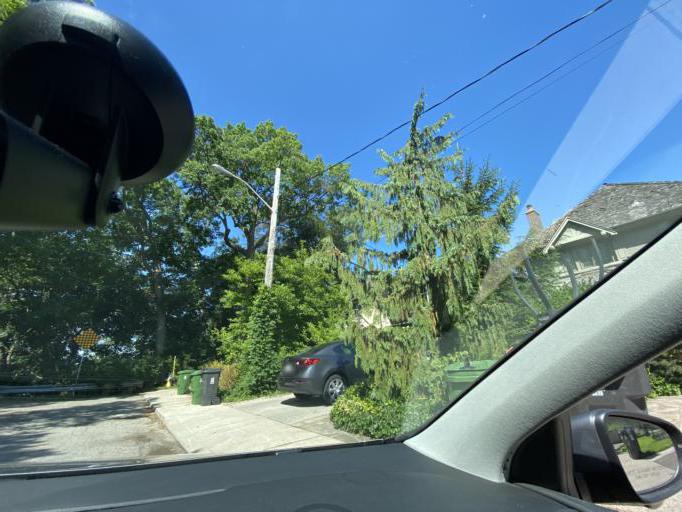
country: CA
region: Ontario
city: Etobicoke
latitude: 43.6587
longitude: -79.4930
